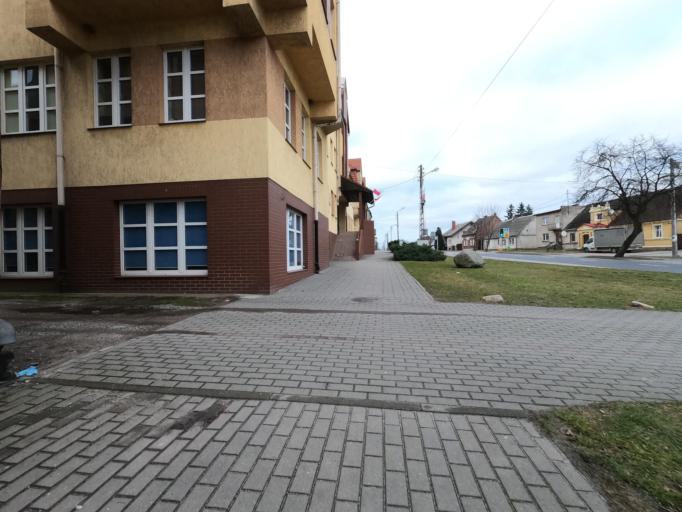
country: PL
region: Greater Poland Voivodeship
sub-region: Powiat pilski
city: Bialosliwie
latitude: 53.1047
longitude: 17.1254
